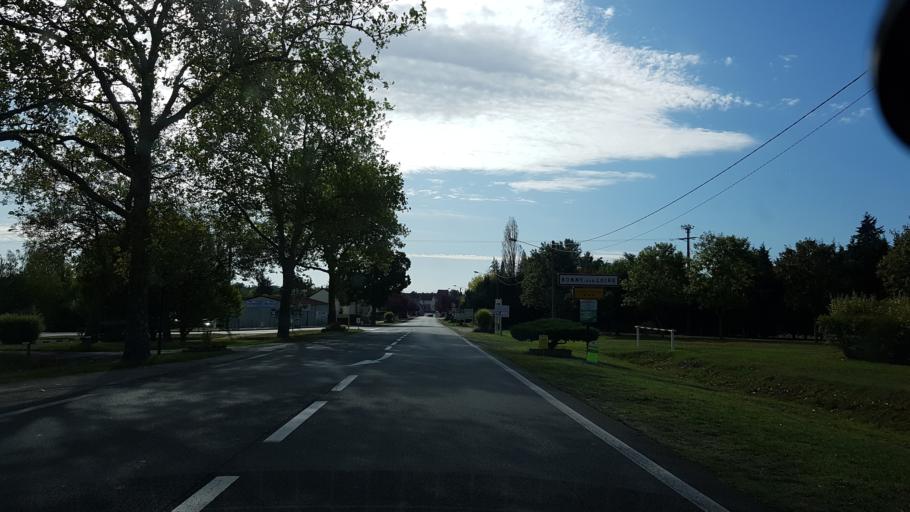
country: FR
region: Centre
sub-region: Departement du Loiret
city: Bonny-sur-Loire
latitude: 47.5661
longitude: 2.8344
